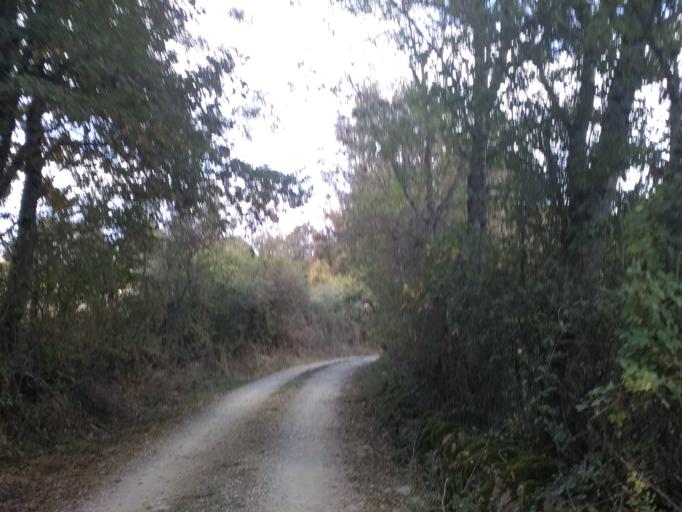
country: FR
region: Midi-Pyrenees
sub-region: Departement de l'Aveyron
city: Bozouls
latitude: 44.4708
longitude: 2.6772
